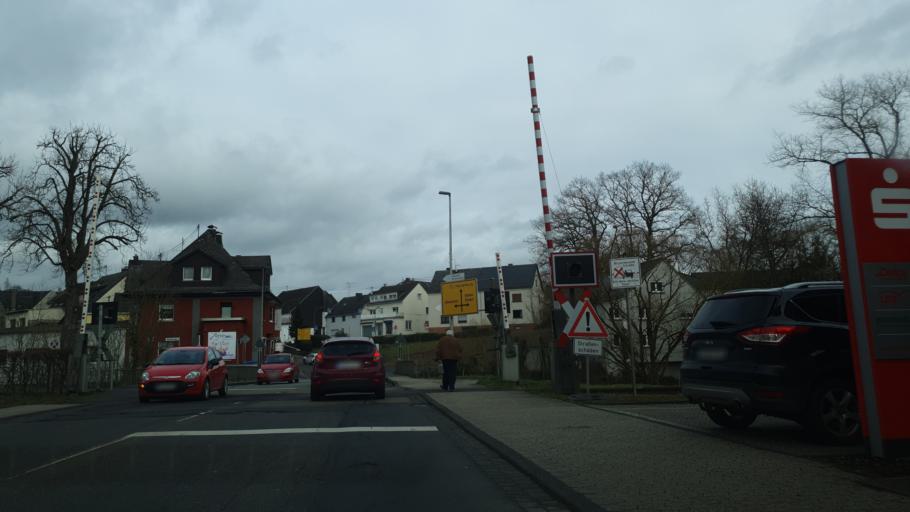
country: DE
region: Rheinland-Pfalz
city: Puderbach
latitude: 50.5982
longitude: 7.6108
